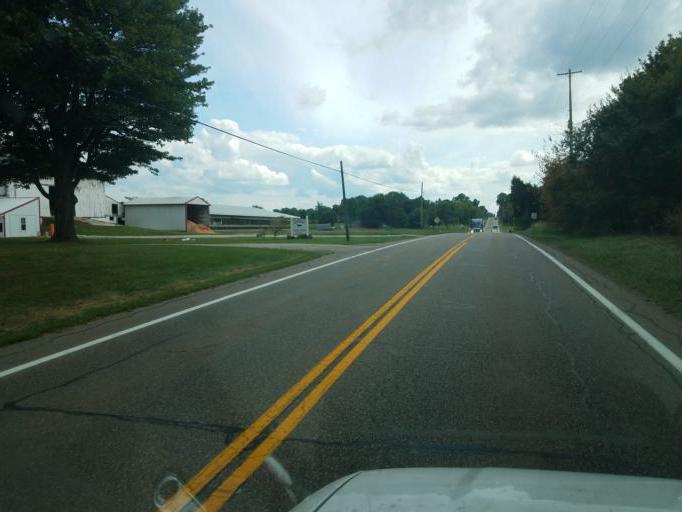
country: US
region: Ohio
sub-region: Stark County
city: Hartville
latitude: 41.0250
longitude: -81.2484
